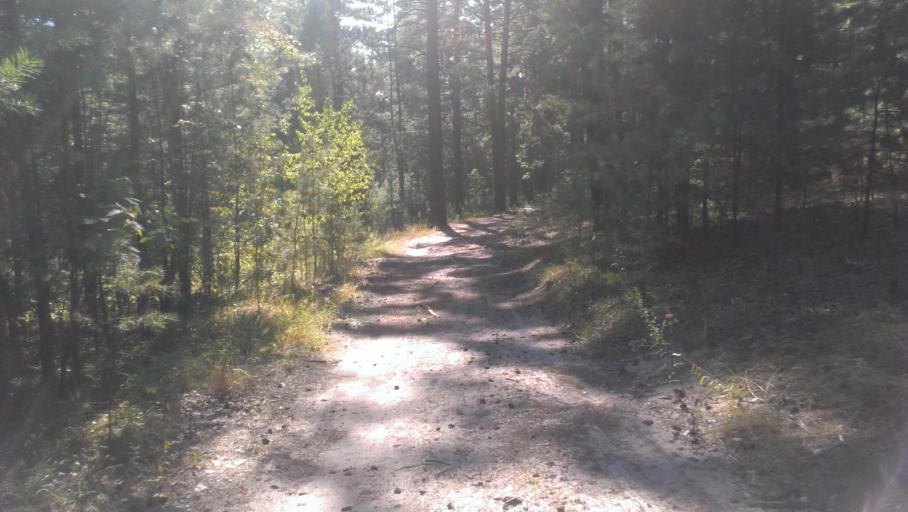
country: RU
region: Altai Krai
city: Yuzhnyy
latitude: 53.3151
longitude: 83.6876
